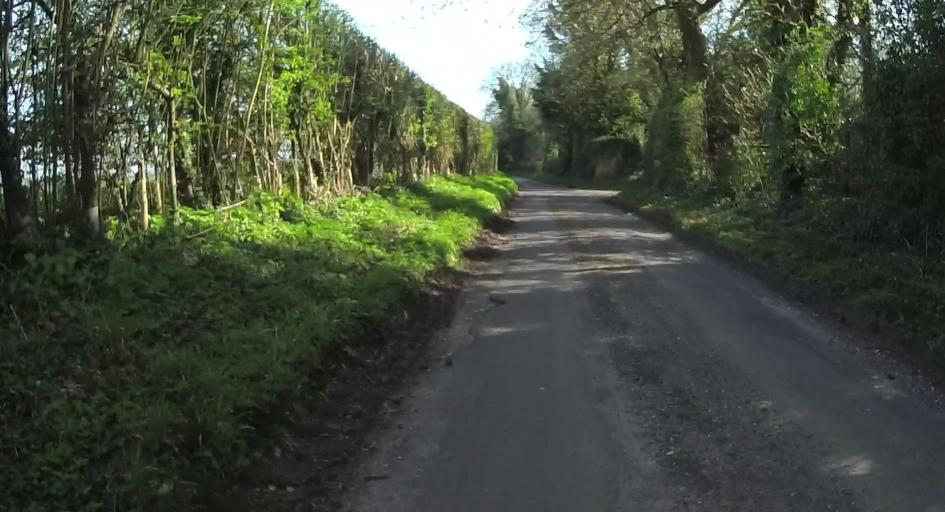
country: GB
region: England
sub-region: Hampshire
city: Highclere
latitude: 51.2631
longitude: -1.3697
